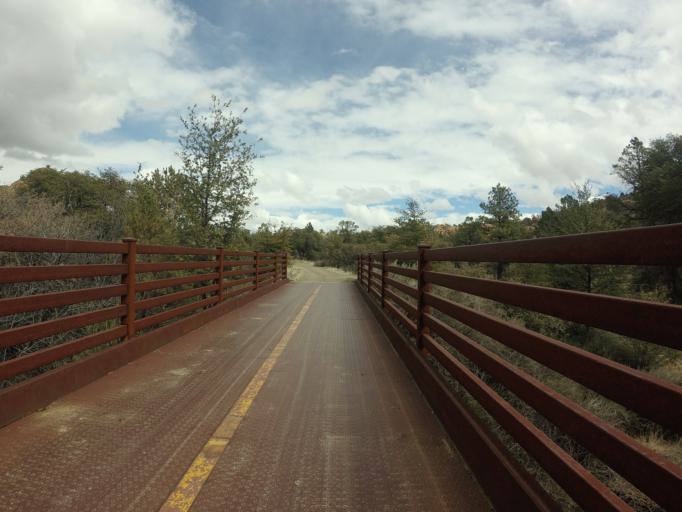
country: US
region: Arizona
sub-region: Yavapai County
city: Prescott Valley
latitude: 34.6043
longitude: -112.3927
